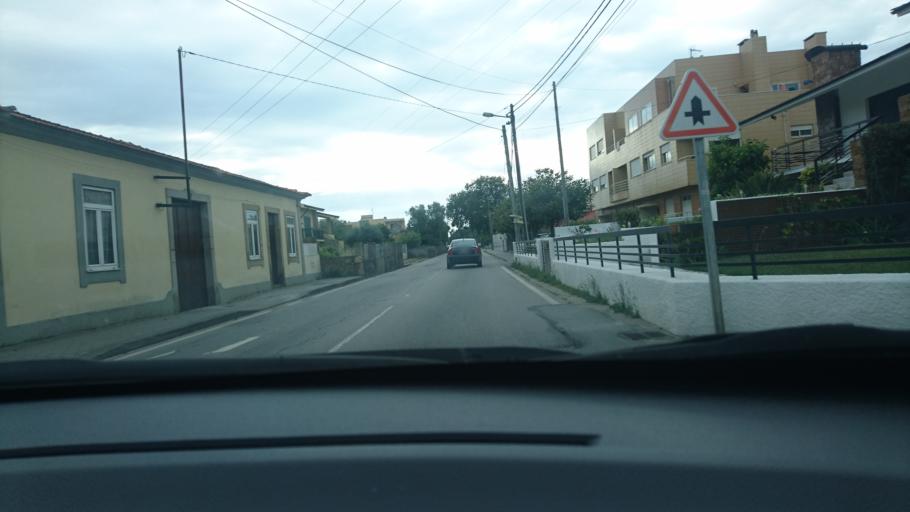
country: PT
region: Aveiro
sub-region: Santa Maria da Feira
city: Rio Meao
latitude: 40.9588
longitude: -8.5910
